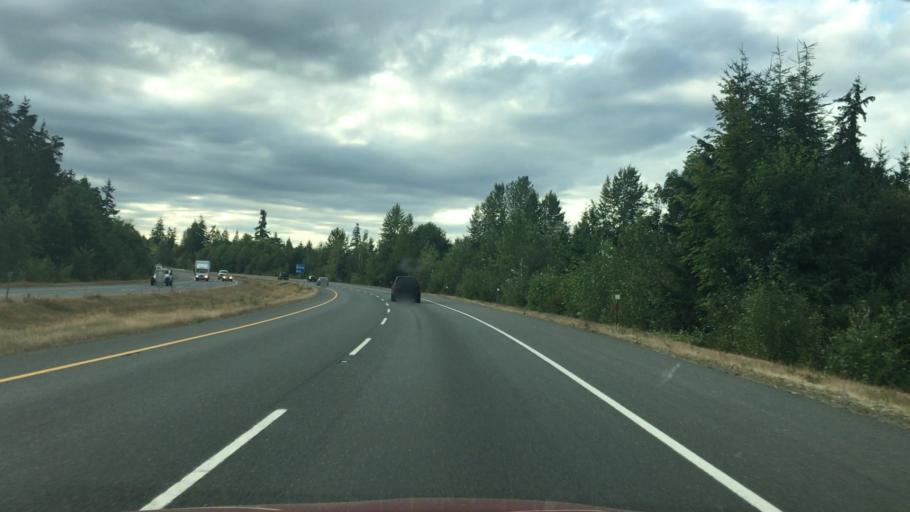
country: CA
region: British Columbia
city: Nanaimo
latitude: 49.1842
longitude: -123.9891
